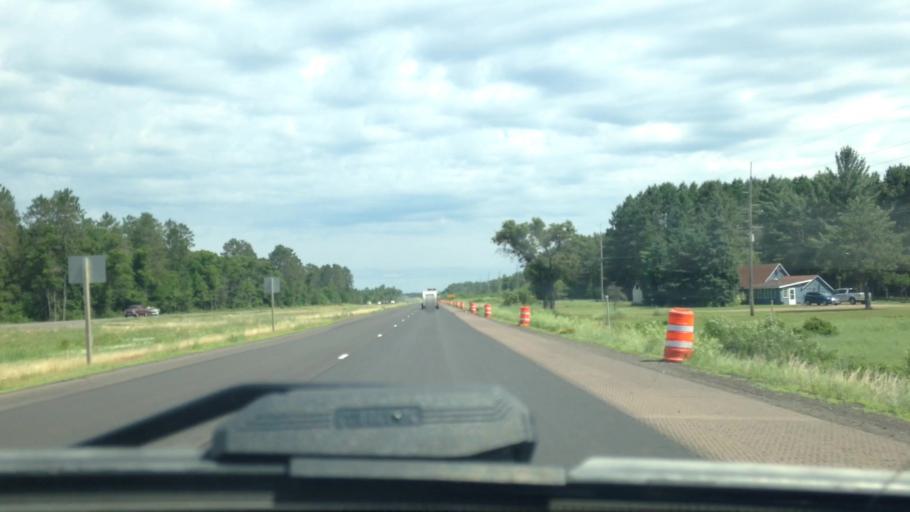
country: US
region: Wisconsin
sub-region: Washburn County
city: Spooner
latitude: 46.1586
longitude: -91.8093
